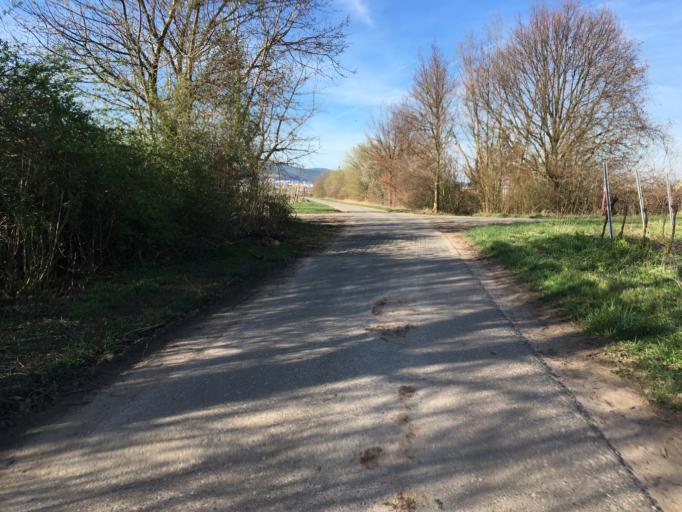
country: DE
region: Rheinland-Pfalz
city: Kirrweiler
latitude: 49.3282
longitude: 8.1587
